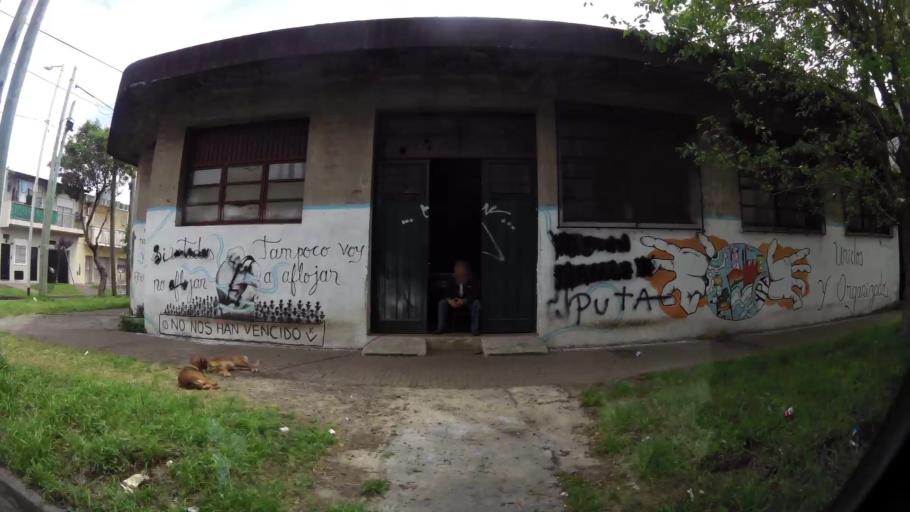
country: AR
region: Buenos Aires
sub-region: Partido de Avellaneda
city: Avellaneda
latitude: -34.6784
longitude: -58.3724
